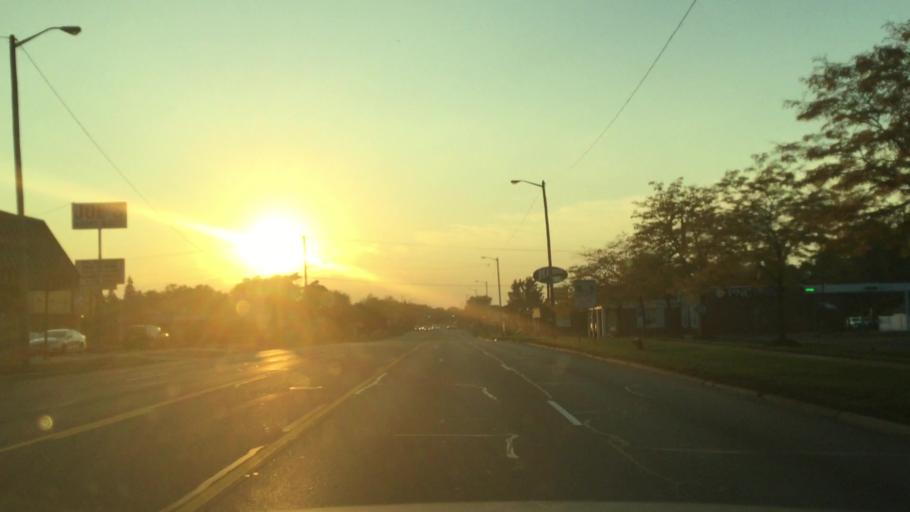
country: US
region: Michigan
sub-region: Oakland County
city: Sylvan Lake
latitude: 42.6352
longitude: -83.3278
